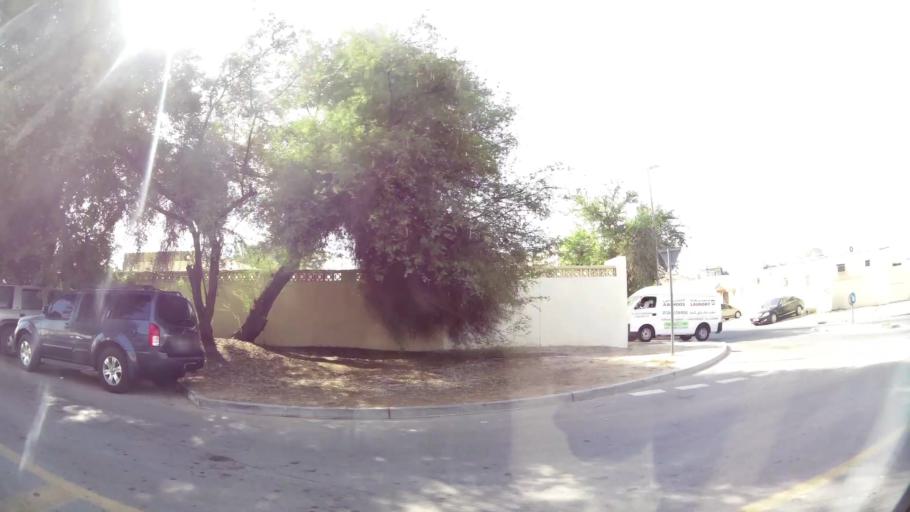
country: AE
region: Ash Shariqah
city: Sharjah
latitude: 25.2618
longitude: 55.4027
